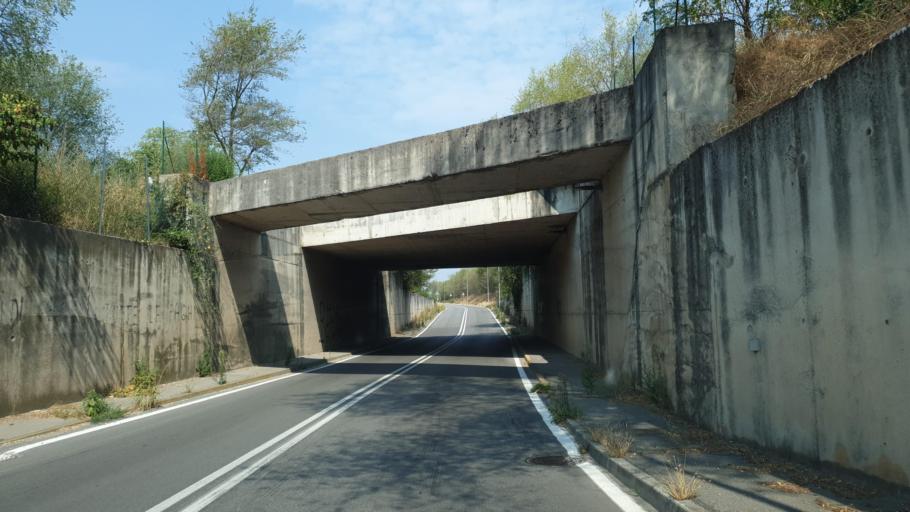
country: IT
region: Lombardy
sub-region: Provincia di Brescia
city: Ghedi
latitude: 45.4285
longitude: 10.2580
